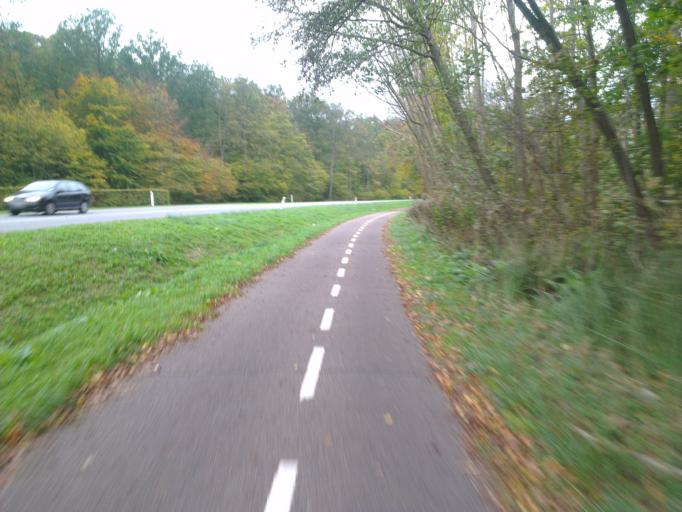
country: DK
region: Capital Region
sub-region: Frederikssund Kommune
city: Frederikssund
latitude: 55.8435
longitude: 12.0303
